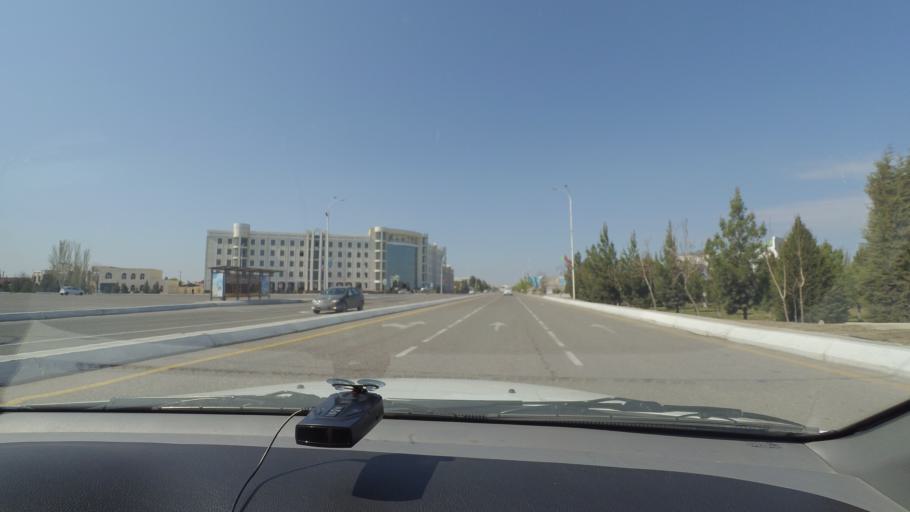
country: UZ
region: Bukhara
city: Bukhara
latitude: 39.7672
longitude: 64.4726
